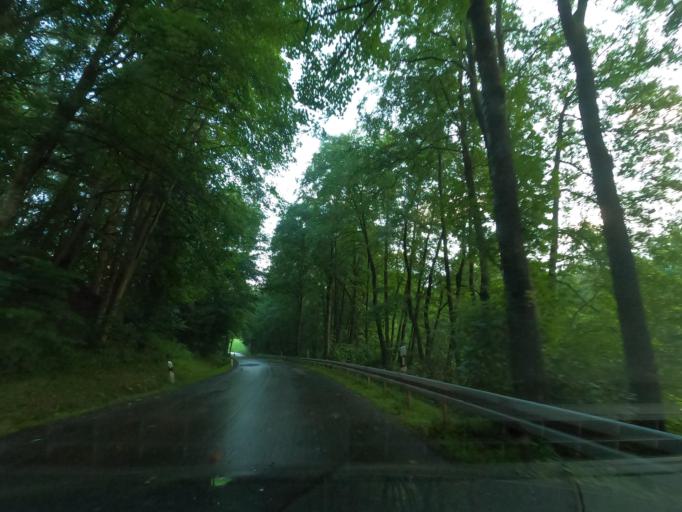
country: DE
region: North Rhine-Westphalia
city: Plettenberg
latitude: 51.2687
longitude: 7.9324
